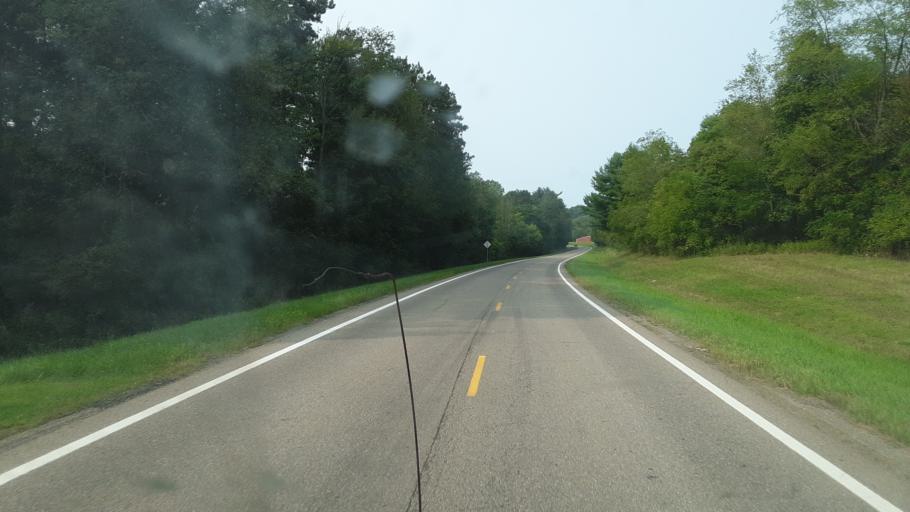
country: US
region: Ohio
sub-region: Knox County
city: Danville
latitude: 40.4631
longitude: -82.2084
